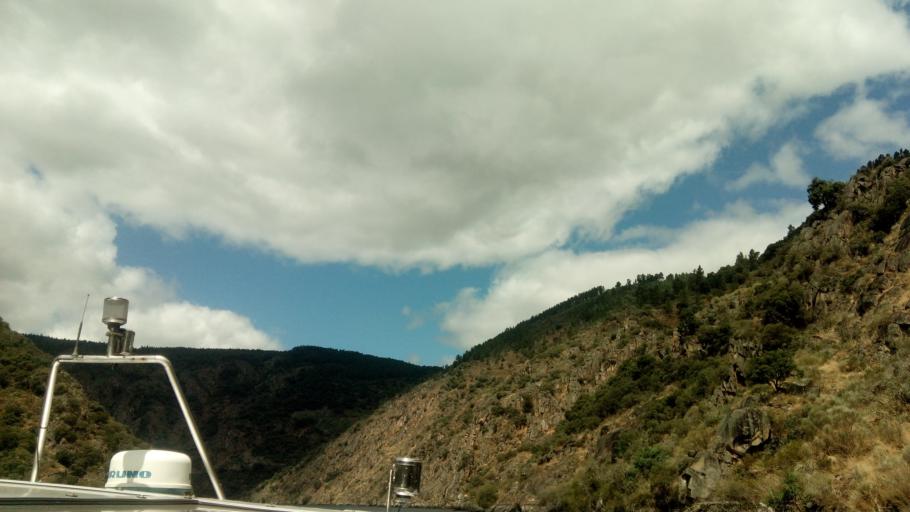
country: ES
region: Galicia
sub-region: Provincia de Lugo
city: Lobios
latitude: 42.3984
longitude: -7.5617
